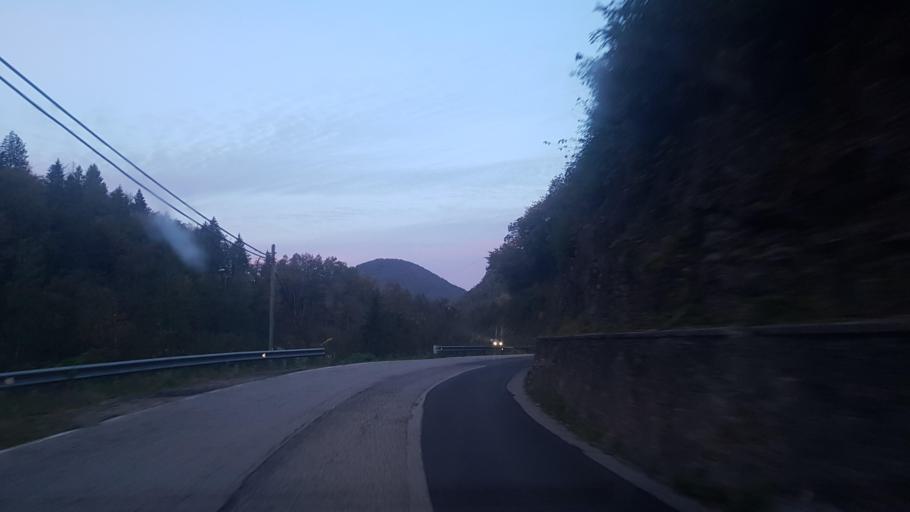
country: IT
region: Friuli Venezia Giulia
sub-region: Provincia di Udine
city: Chiaulis
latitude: 46.3865
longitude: 12.9997
